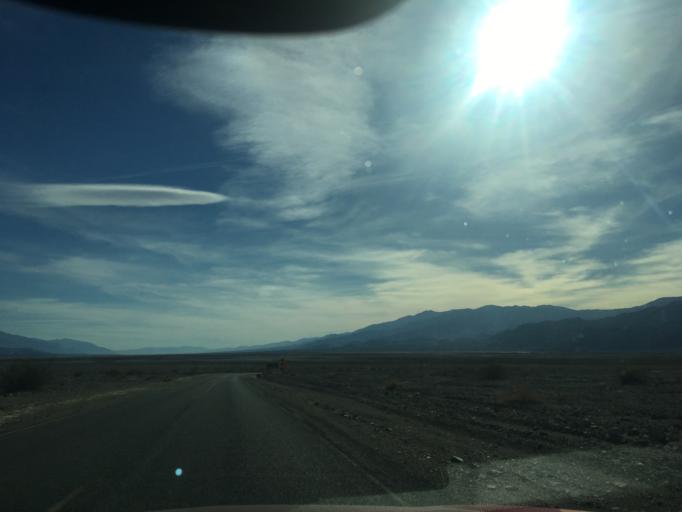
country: US
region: Nevada
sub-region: Nye County
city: Beatty
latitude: 36.5908
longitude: -116.9433
